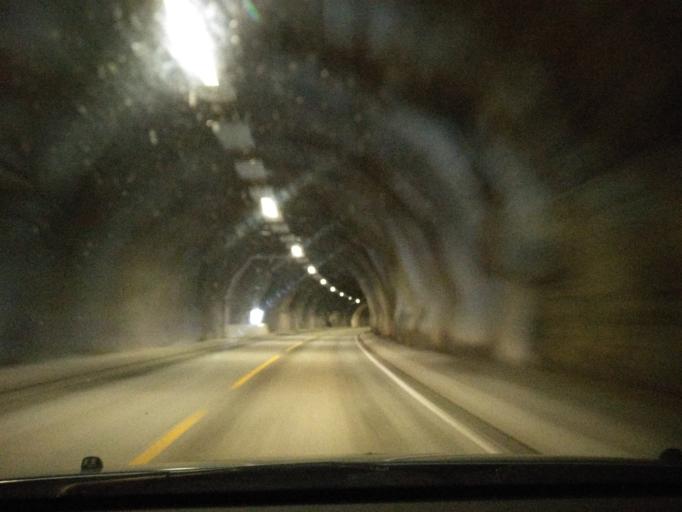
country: NO
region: Rogaland
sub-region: Sauda
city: Sauda
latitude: 59.8638
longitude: 6.3617
